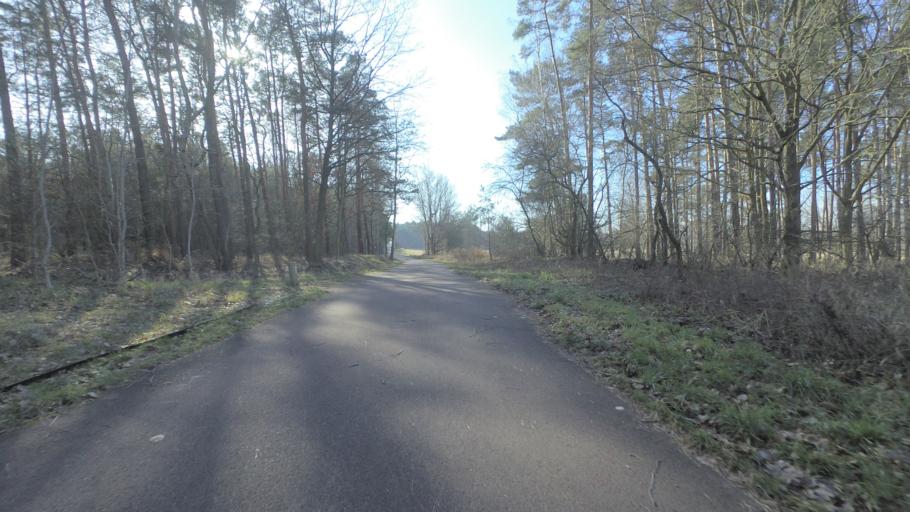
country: DE
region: Brandenburg
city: Juterbog
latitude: 52.0262
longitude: 13.1297
